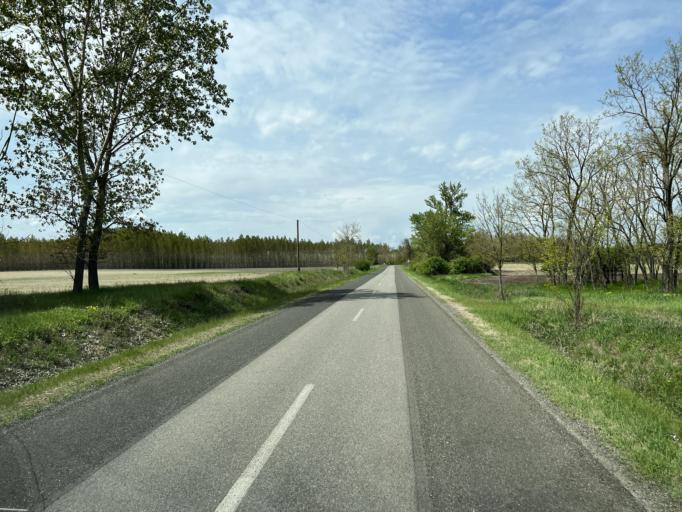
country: HU
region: Pest
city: Albertirsa
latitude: 47.1658
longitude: 19.6161
